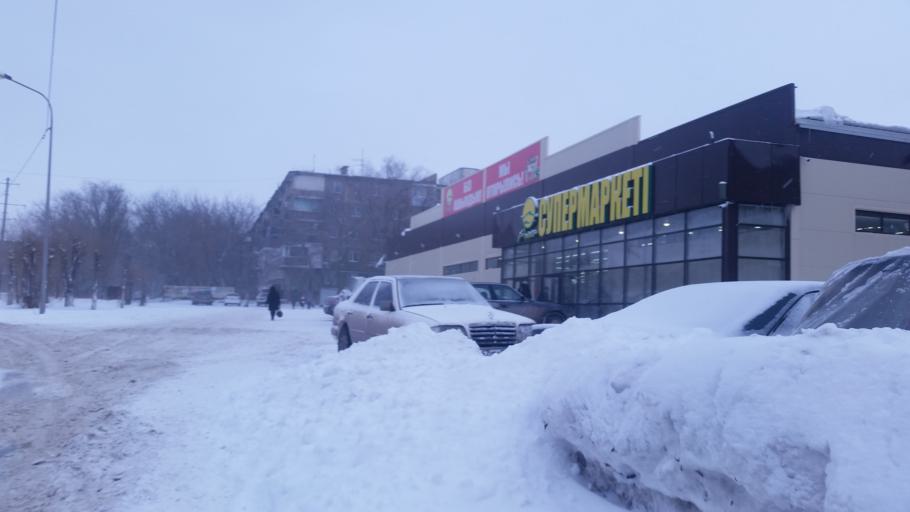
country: KZ
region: Qaraghandy
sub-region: Qaraghandy Qalasy
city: Karagandy
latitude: 49.7695
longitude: 73.1496
